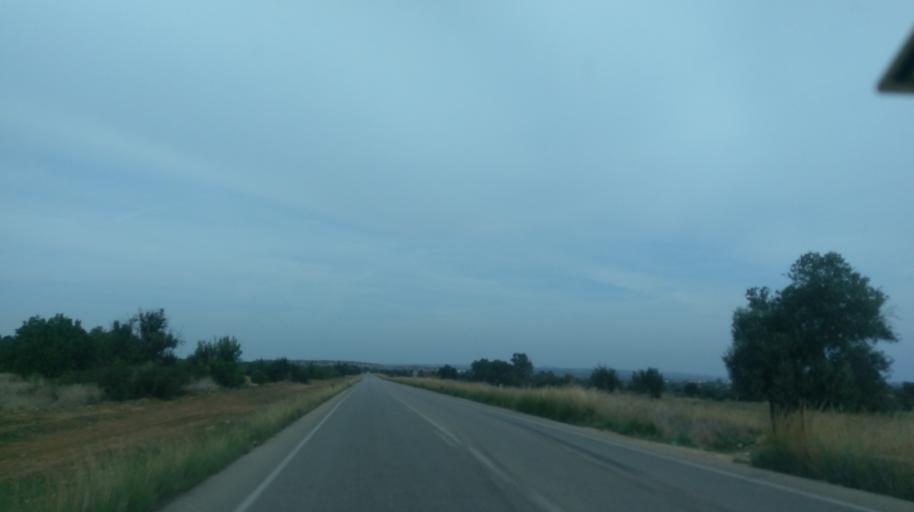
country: CY
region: Ammochostos
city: Leonarisso
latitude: 35.4038
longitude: 34.1067
